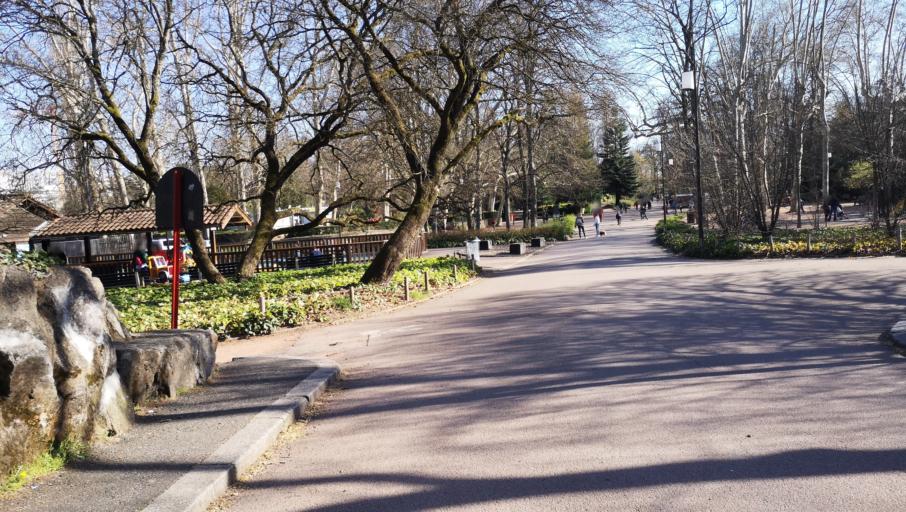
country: FR
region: Rhone-Alpes
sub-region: Departement du Rhone
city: Caluire-et-Cuire
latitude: 45.7812
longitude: 4.8561
